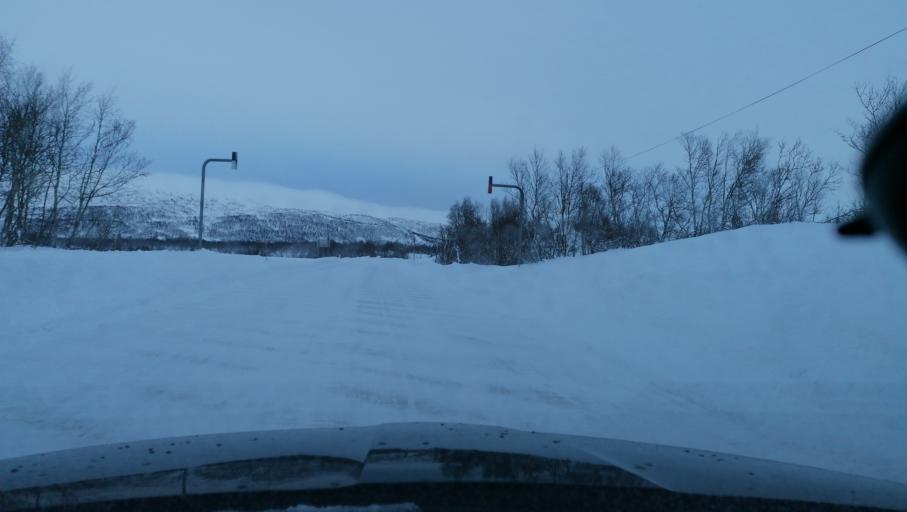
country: NO
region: Aust-Agder
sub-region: Bykle
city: Hovden
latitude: 59.6428
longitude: 7.4583
